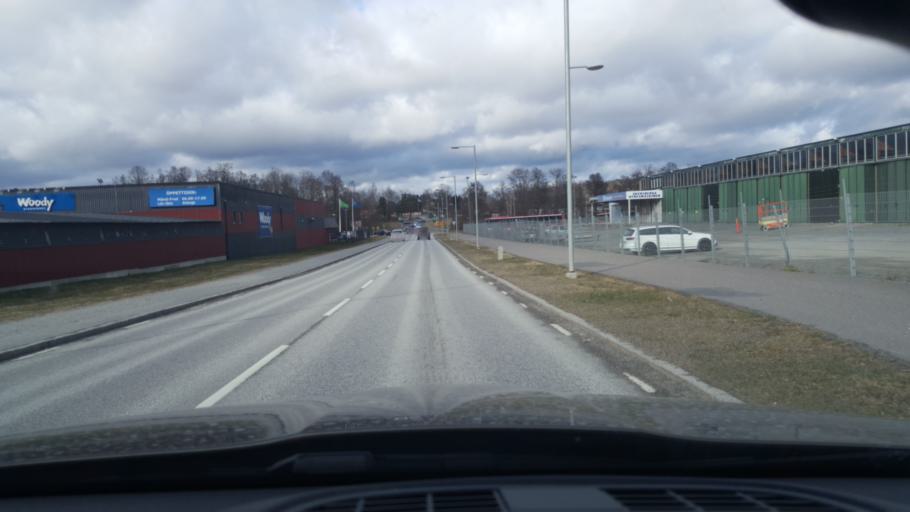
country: SE
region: Stockholm
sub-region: Osterakers Kommun
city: Akersberga
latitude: 59.4918
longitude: 18.2756
